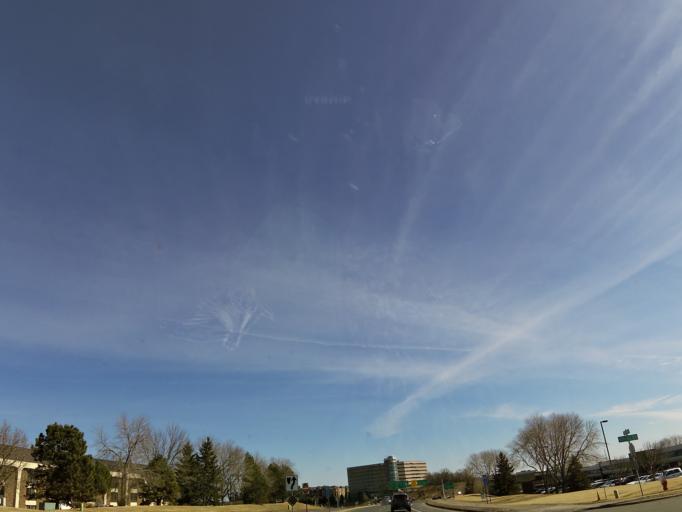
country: US
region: Minnesota
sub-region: Hennepin County
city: Eden Prairie
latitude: 44.8643
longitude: -93.4228
